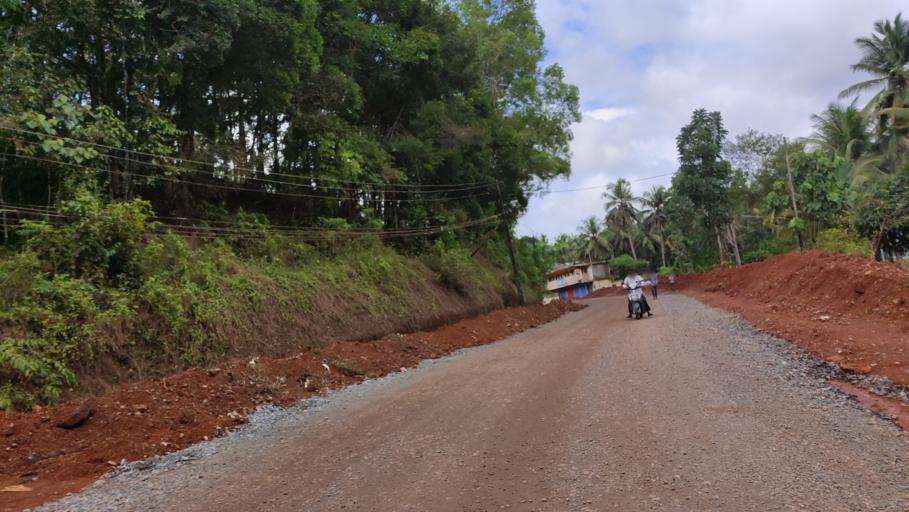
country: IN
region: Kerala
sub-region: Kasaragod District
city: Kasaragod
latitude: 12.5221
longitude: 75.0721
